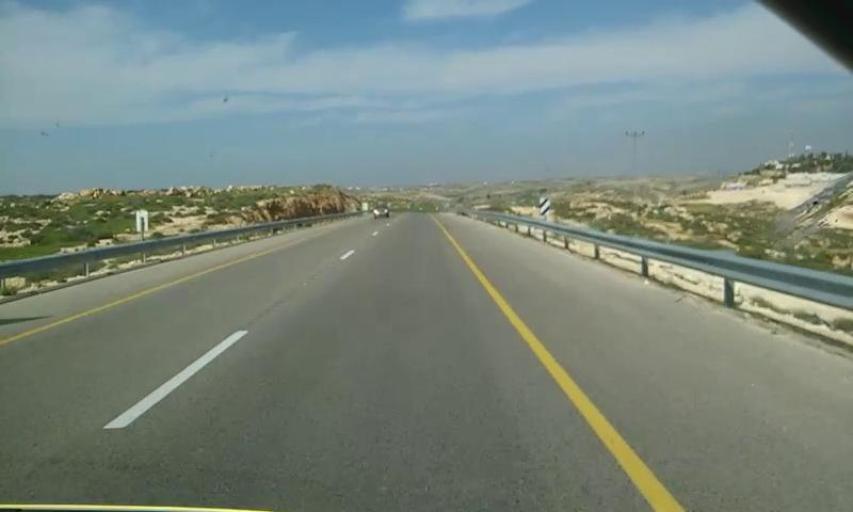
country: PS
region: West Bank
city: Az Zahiriyah
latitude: 31.3823
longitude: 35.0050
